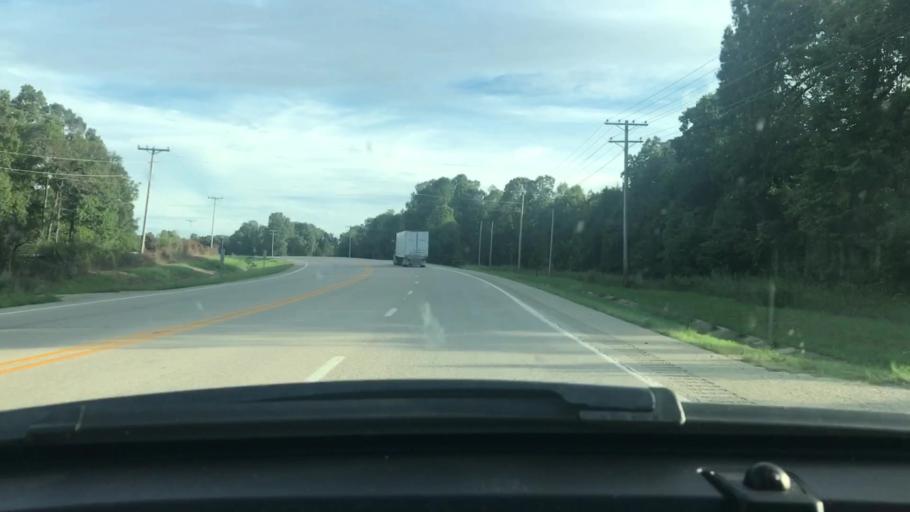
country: US
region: Arkansas
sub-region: Lawrence County
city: Hoxie
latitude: 36.1315
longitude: -91.1584
